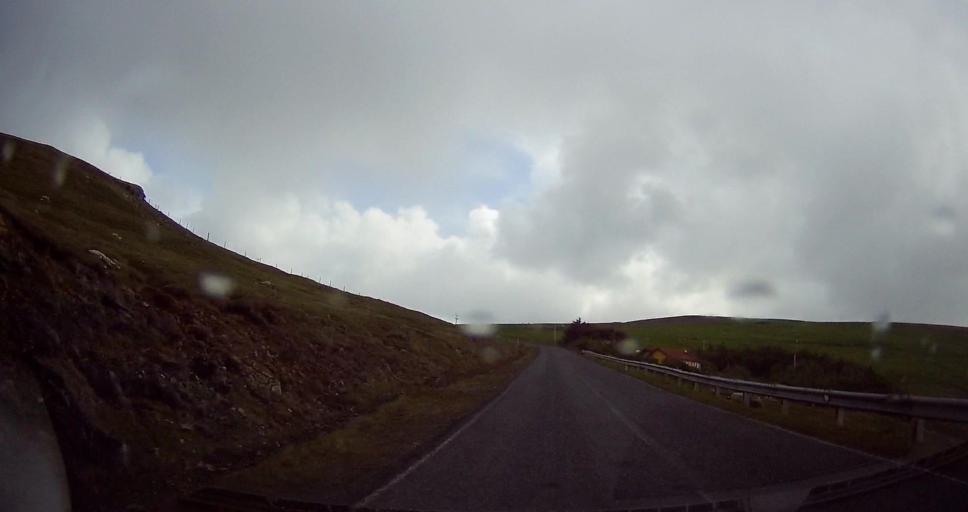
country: GB
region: Scotland
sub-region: Shetland Islands
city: Lerwick
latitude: 60.5411
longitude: -1.3499
